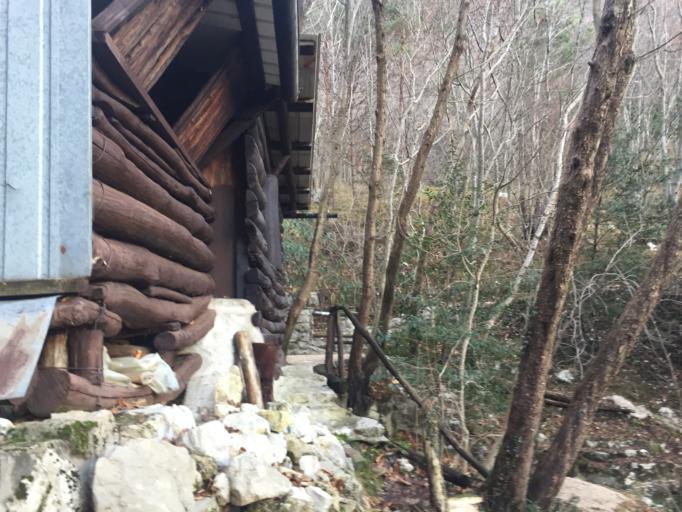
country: IT
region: Friuli Venezia Giulia
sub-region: Provincia di Udine
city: Trasaghis
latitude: 46.2873
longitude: 13.0841
